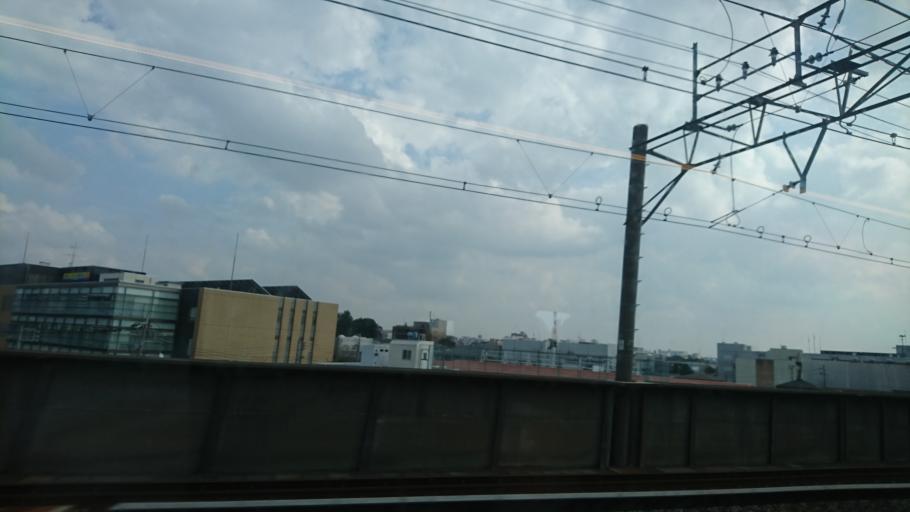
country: JP
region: Saitama
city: Yono
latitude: 35.8857
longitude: 139.6254
